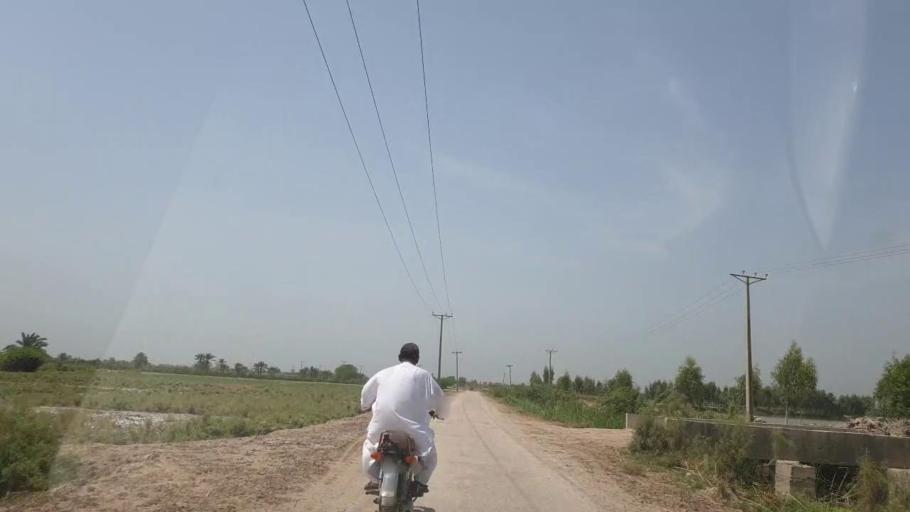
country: PK
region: Sindh
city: Ranipur
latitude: 27.3067
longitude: 68.5460
